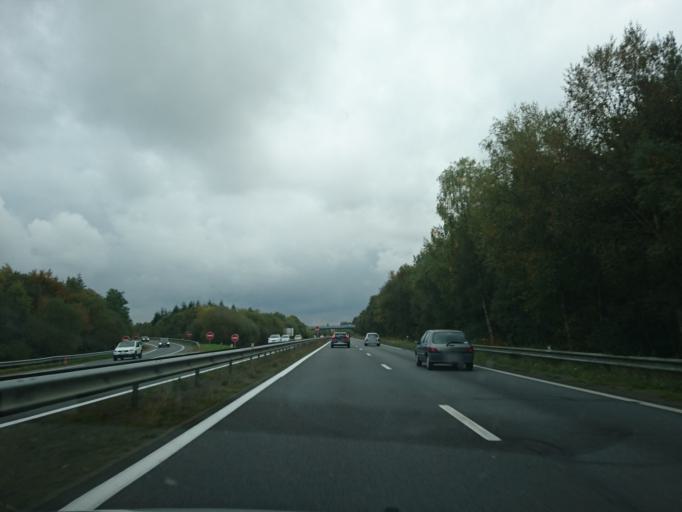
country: FR
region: Brittany
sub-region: Departement des Cotes-d'Armor
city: Plestan
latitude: 48.4063
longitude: -2.4176
